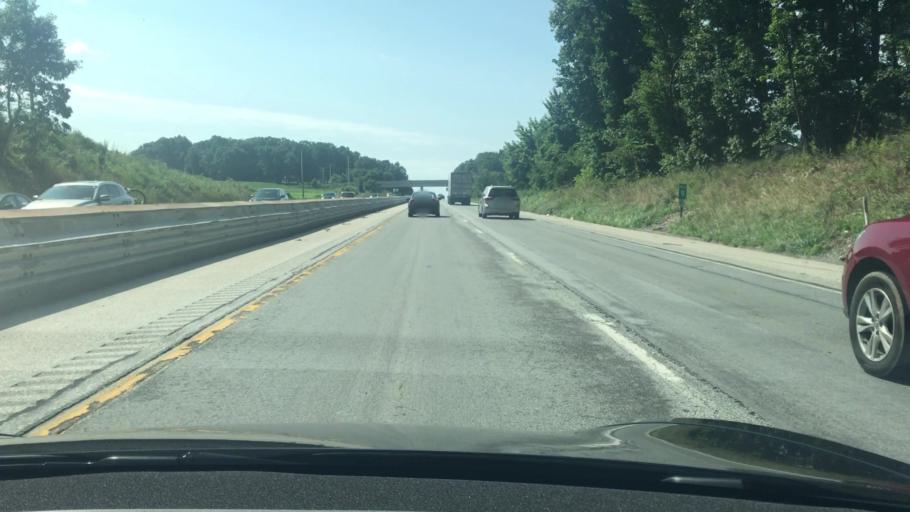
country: US
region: Pennsylvania
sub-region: York County
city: Loganville
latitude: 39.8483
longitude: -76.6893
